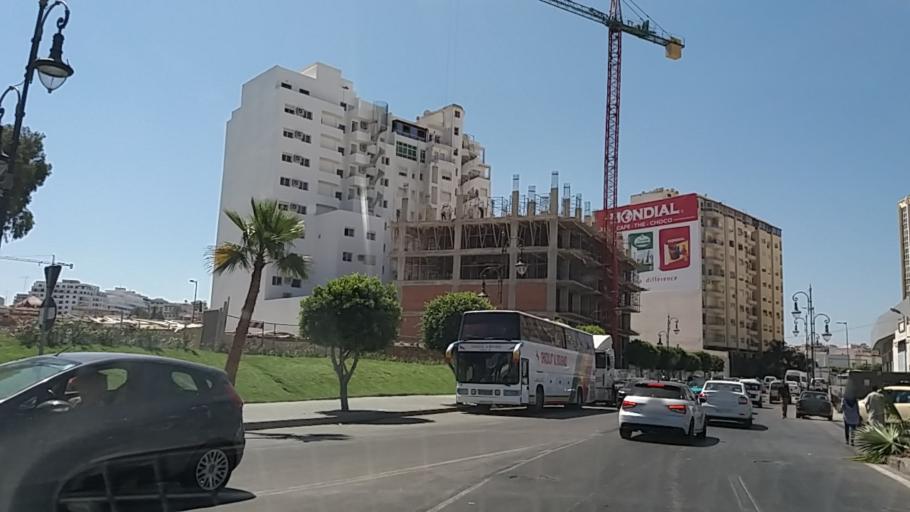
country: MA
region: Tanger-Tetouan
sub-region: Tanger-Assilah
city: Tangier
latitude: 35.7694
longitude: -5.8036
